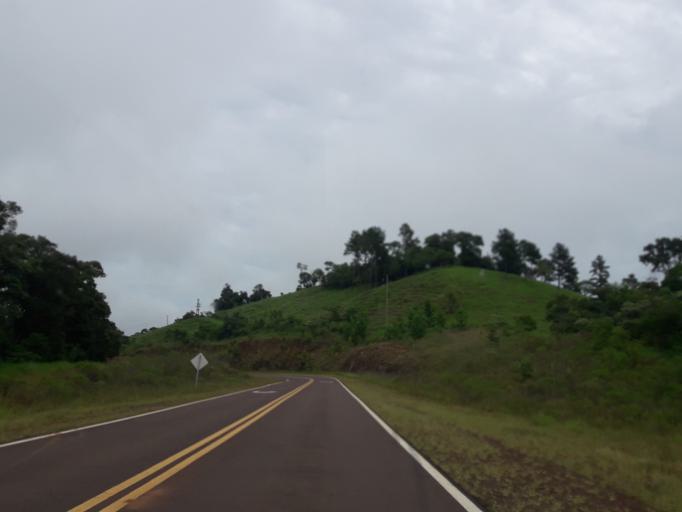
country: AR
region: Misiones
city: Bernardo de Irigoyen
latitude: -26.3961
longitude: -53.8121
